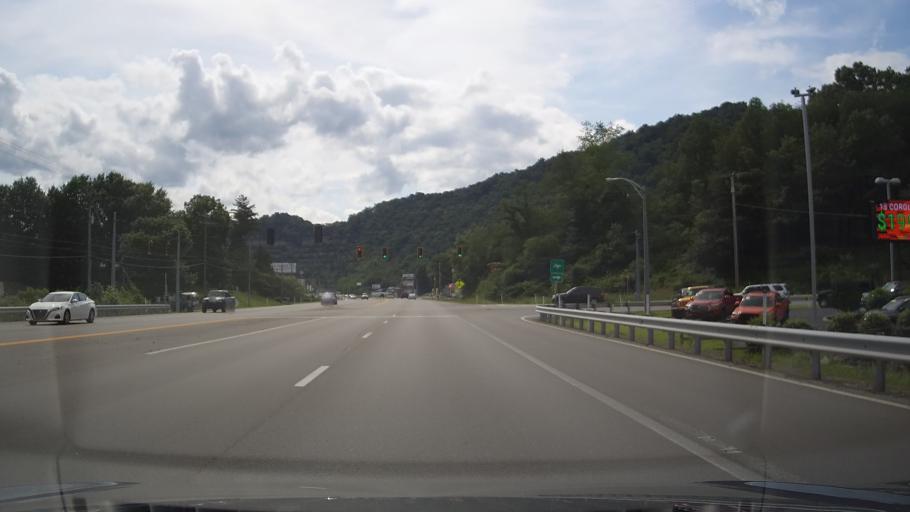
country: US
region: Kentucky
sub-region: Pike County
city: Coal Run Village
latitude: 37.5368
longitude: -82.6007
